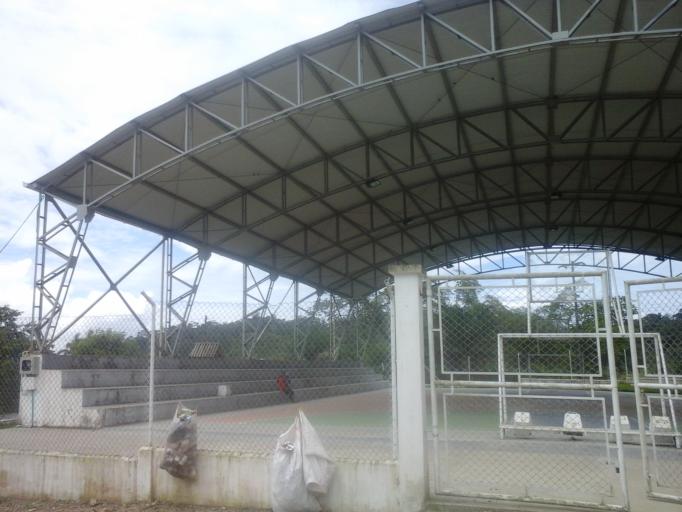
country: CO
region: Putumayo
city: Mocoa
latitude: 1.1840
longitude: -76.6759
